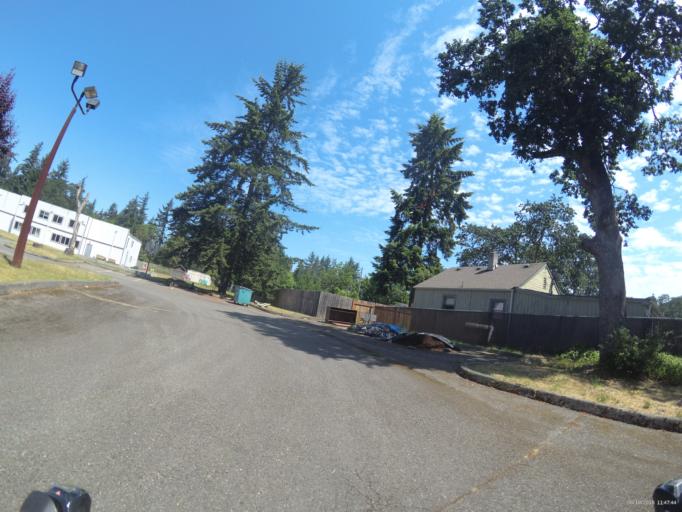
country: US
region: Washington
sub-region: Pierce County
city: Lakewood
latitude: 47.1799
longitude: -122.5253
